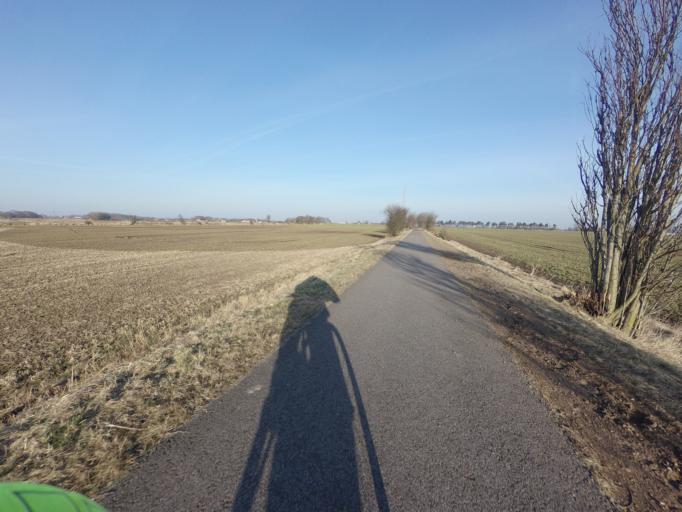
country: SE
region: Skane
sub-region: Hoganas Kommun
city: Hoganas
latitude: 56.1909
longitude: 12.6174
